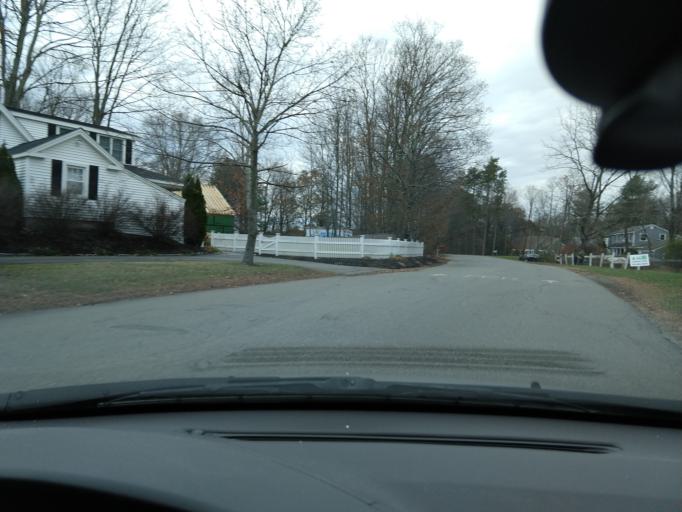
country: US
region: Massachusetts
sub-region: Middlesex County
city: Westford
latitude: 42.5853
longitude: -71.4351
